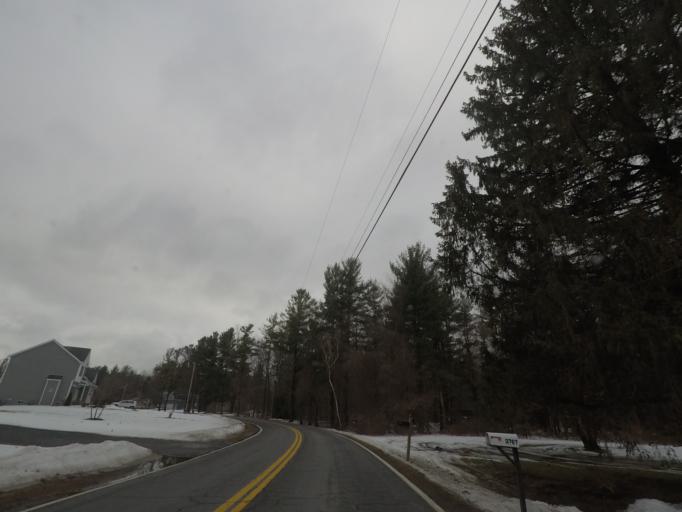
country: US
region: New York
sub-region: Schenectady County
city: Rotterdam
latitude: 42.7464
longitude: -73.9641
